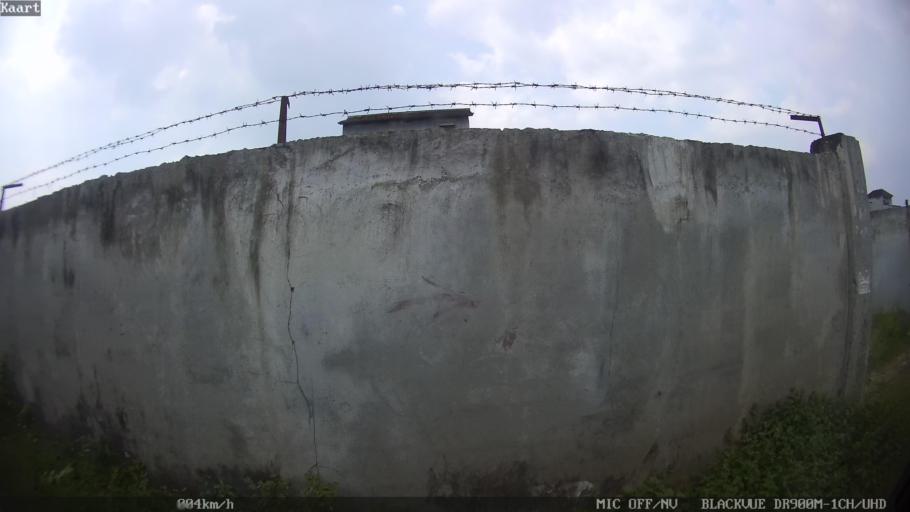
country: ID
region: Lampung
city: Gadingrejo
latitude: -5.3716
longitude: 105.0653
